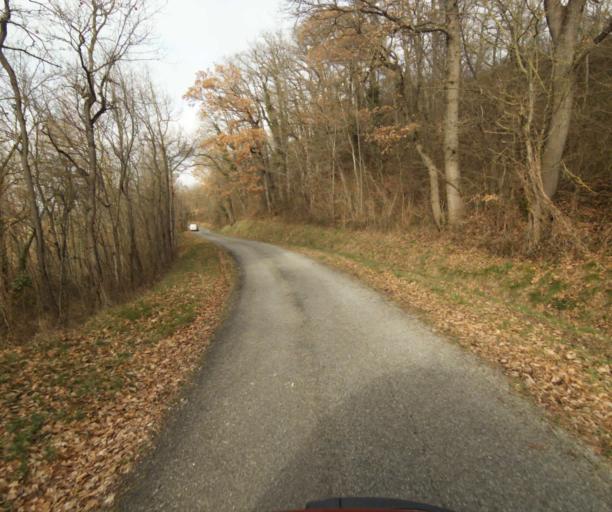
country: FR
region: Languedoc-Roussillon
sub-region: Departement de l'Aude
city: Belpech
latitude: 43.1647
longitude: 1.7380
